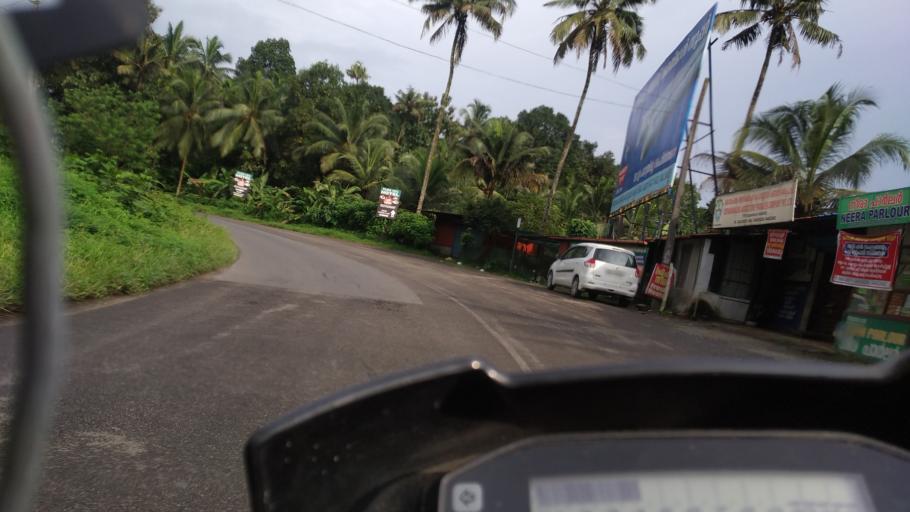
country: IN
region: Kerala
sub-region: Ernakulam
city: Kotamangalam
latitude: 10.0520
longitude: 76.7058
